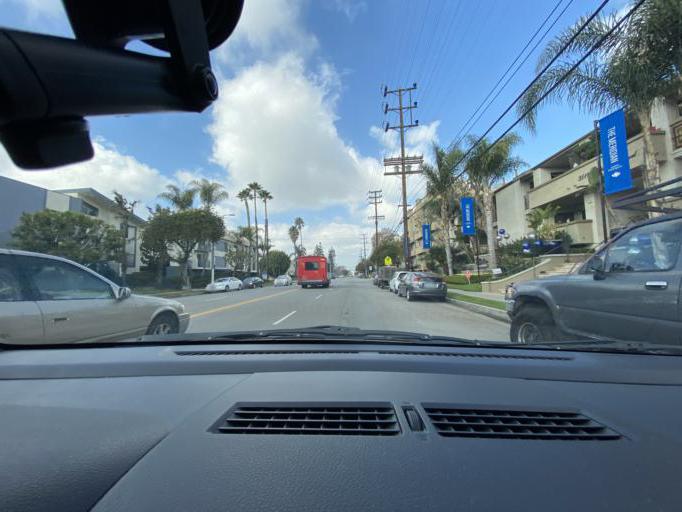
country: US
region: California
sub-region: Los Angeles County
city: Culver City
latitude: 34.0162
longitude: -118.4235
